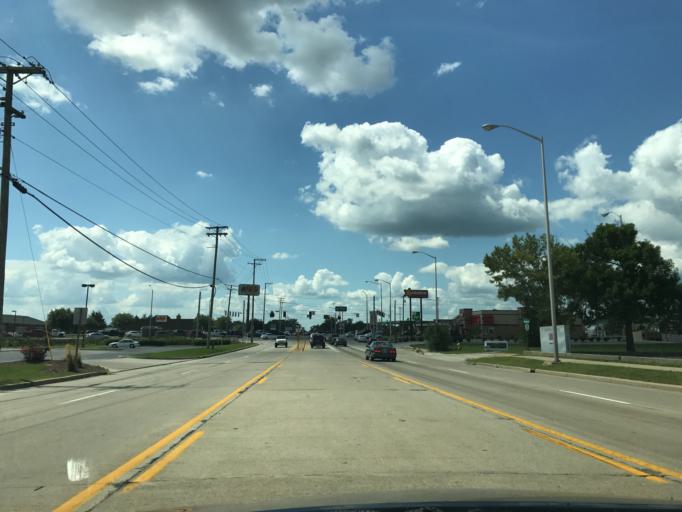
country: US
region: Indiana
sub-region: Allen County
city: Fort Wayne
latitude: 41.1324
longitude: -85.1582
